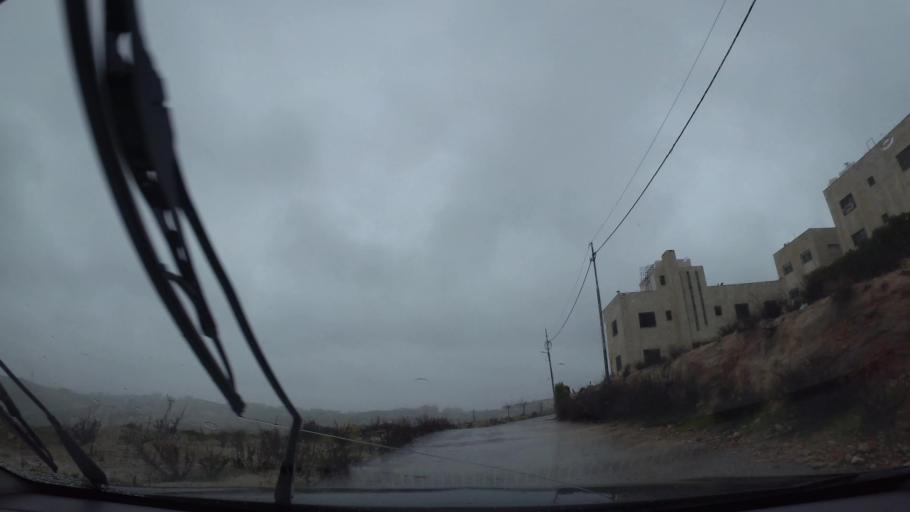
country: JO
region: Amman
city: Al Jubayhah
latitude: 32.0088
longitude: 35.9008
